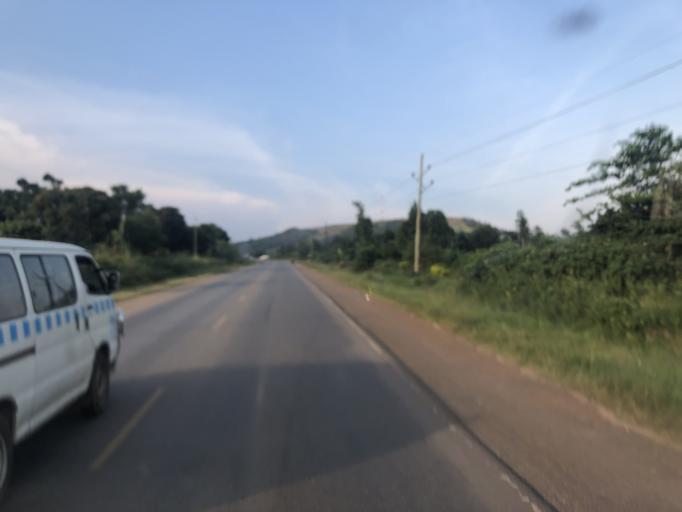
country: UG
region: Central Region
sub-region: Mpigi District
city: Mpigi
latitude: 0.1882
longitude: 32.2912
